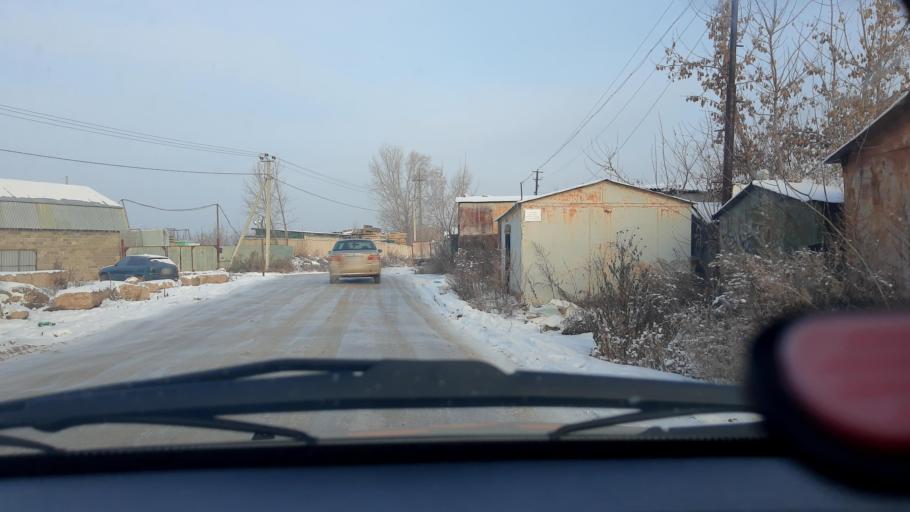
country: RU
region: Bashkortostan
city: Mikhaylovka
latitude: 54.7715
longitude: 55.9132
